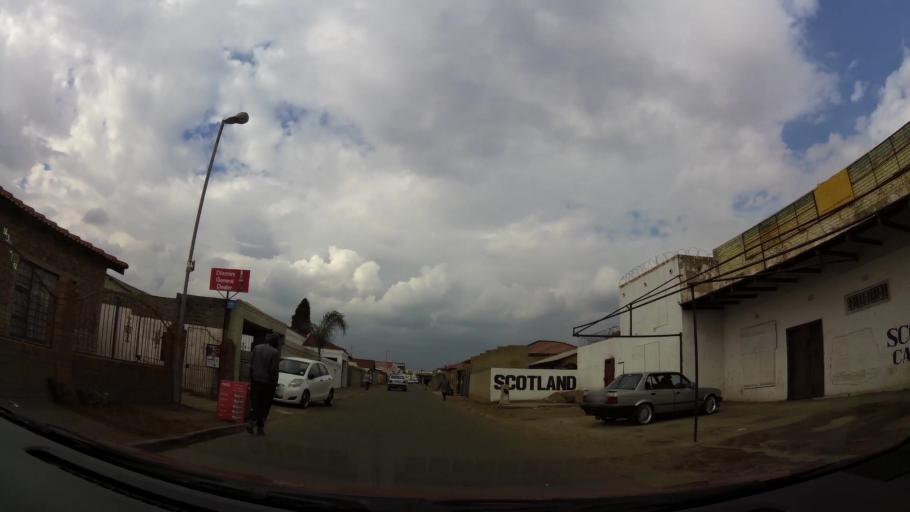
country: ZA
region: Gauteng
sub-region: City of Johannesburg Metropolitan Municipality
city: Soweto
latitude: -26.2491
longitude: 27.8517
